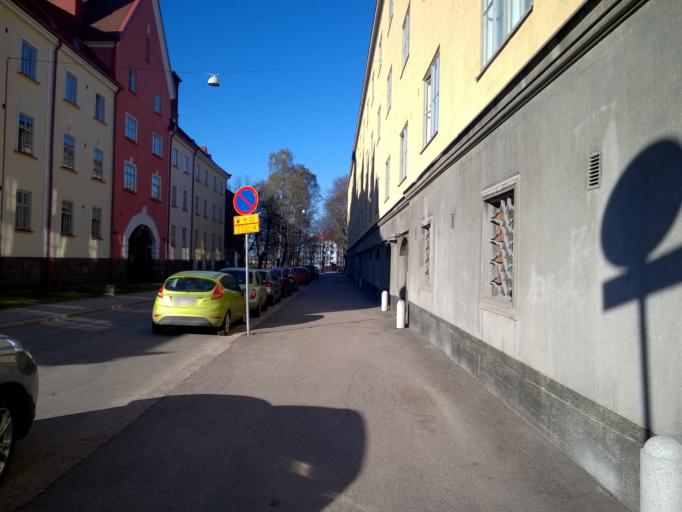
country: FI
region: Uusimaa
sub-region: Helsinki
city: Helsinki
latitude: 60.1964
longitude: 24.9591
